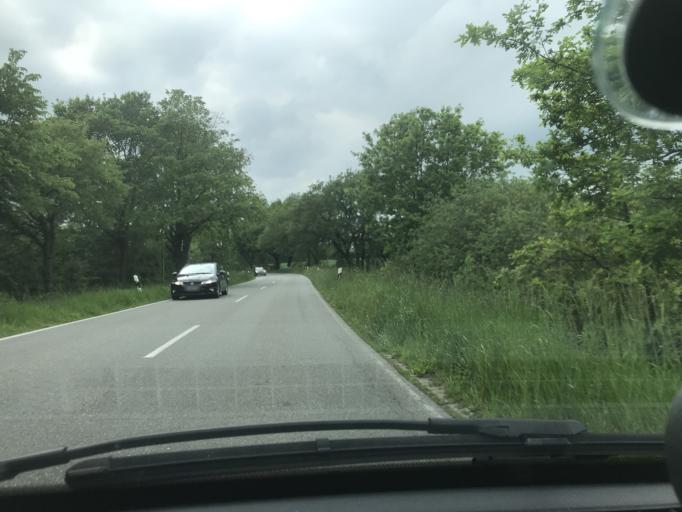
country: DE
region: Schleswig-Holstein
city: Grossensee
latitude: 53.6131
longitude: 10.3229
